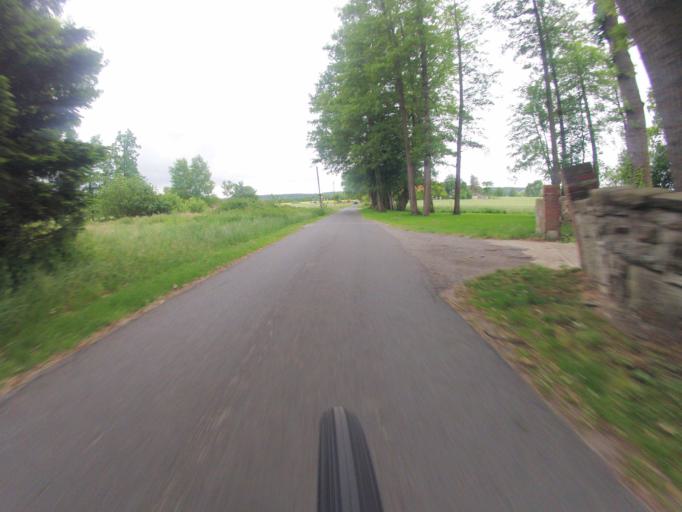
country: DE
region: North Rhine-Westphalia
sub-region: Regierungsbezirk Munster
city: Tecklenburg
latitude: 52.2542
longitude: 7.7732
